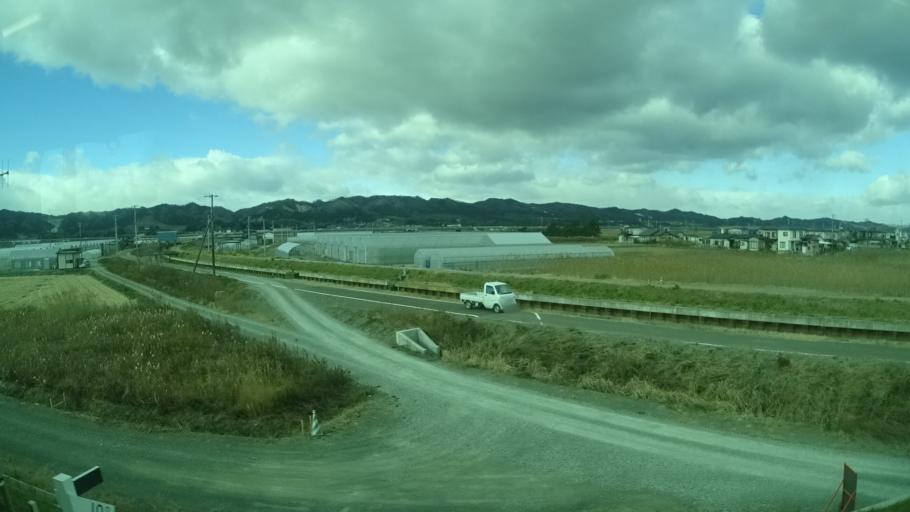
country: JP
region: Miyagi
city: Watari
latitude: 37.9867
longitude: 140.8906
